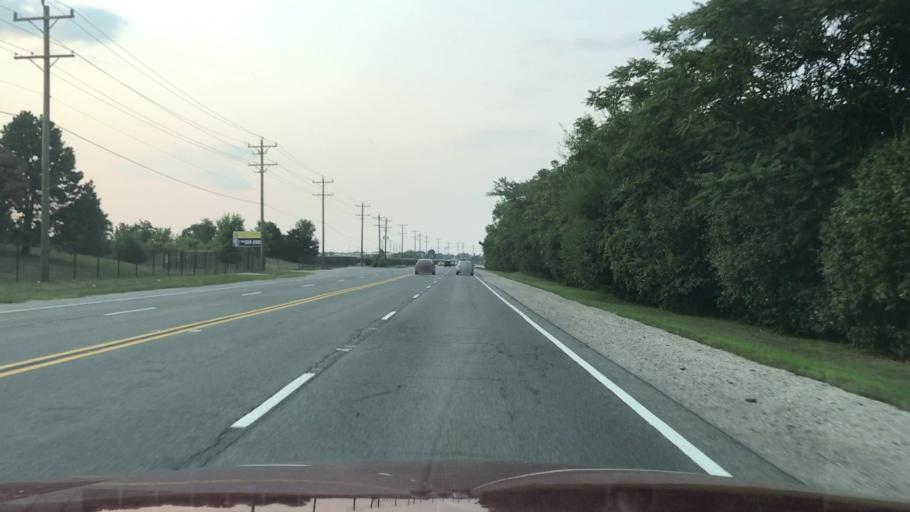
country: US
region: Illinois
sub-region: Will County
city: Romeoville
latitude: 41.6202
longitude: -88.0788
